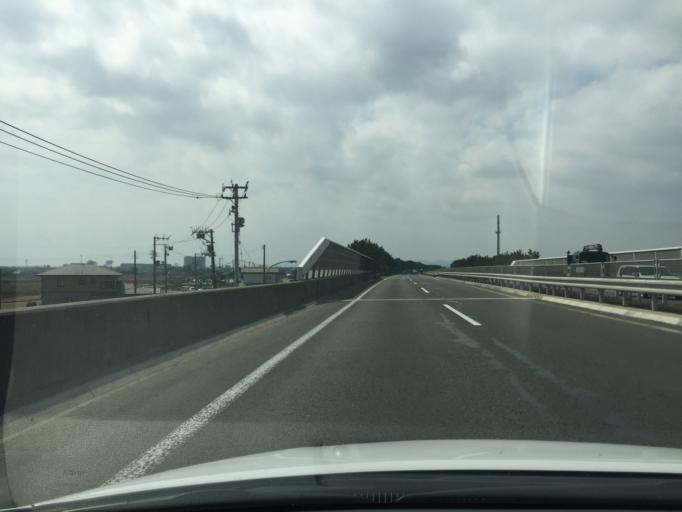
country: JP
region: Miyagi
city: Iwanuma
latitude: 38.1758
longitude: 140.9259
